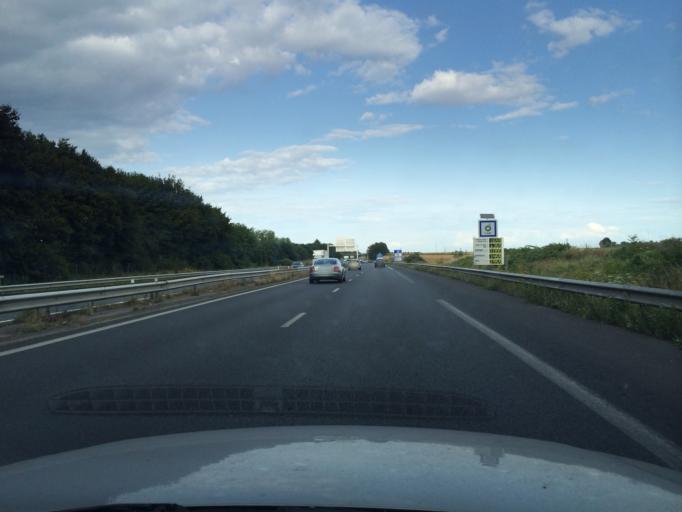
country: FR
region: Lower Normandy
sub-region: Departement du Calvados
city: Giberville
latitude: 49.1670
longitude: -0.2897
